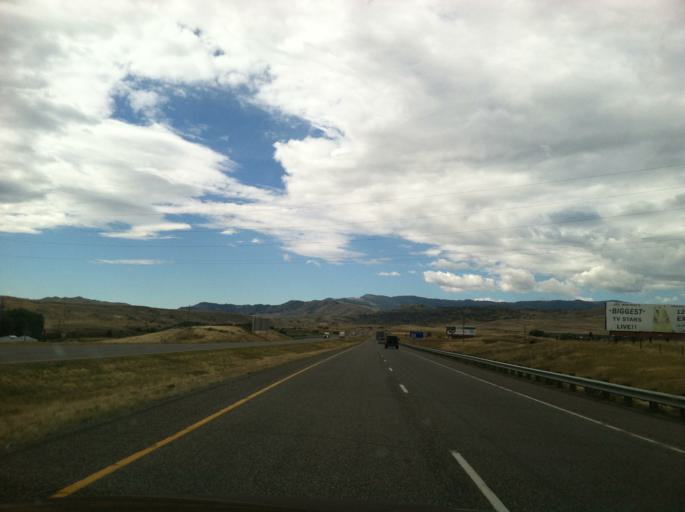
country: US
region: Montana
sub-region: Park County
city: Livingston
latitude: 45.6489
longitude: -110.6046
